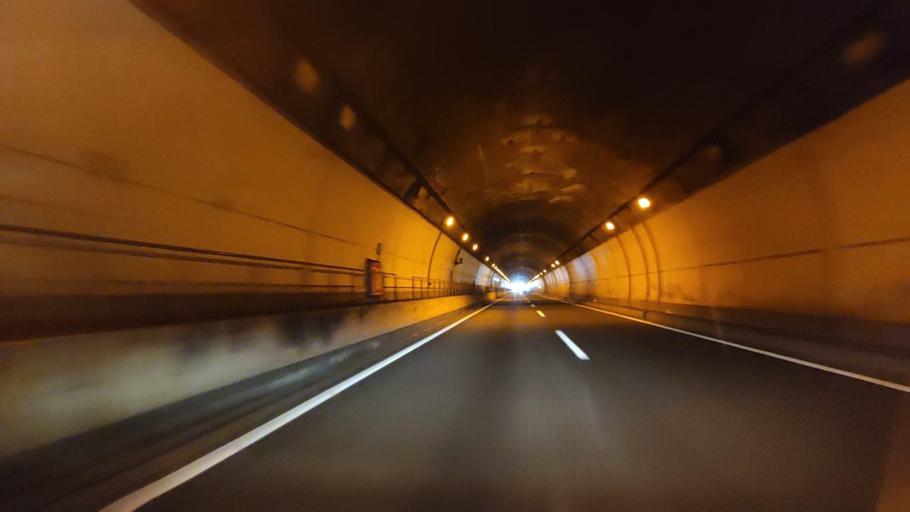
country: JP
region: Akita
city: Hanawa
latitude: 40.0127
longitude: 140.9874
